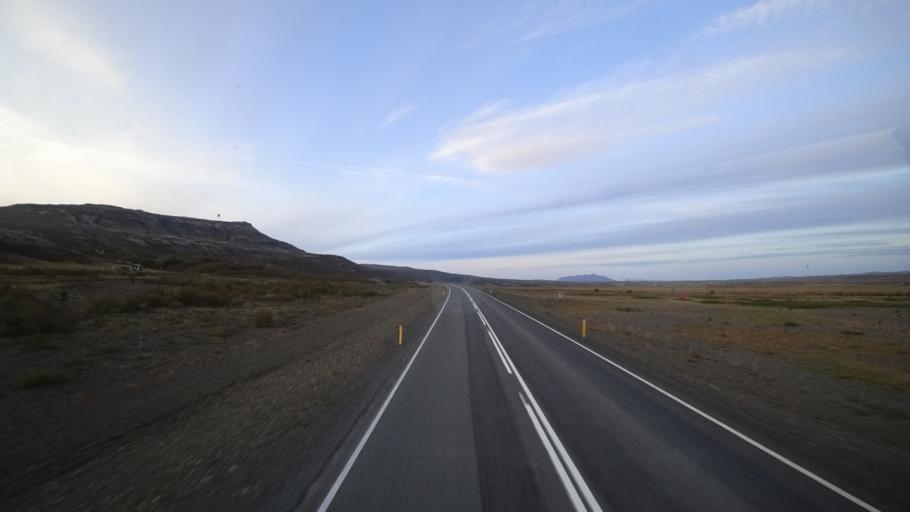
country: IS
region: South
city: Selfoss
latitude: 64.2835
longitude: -20.3423
